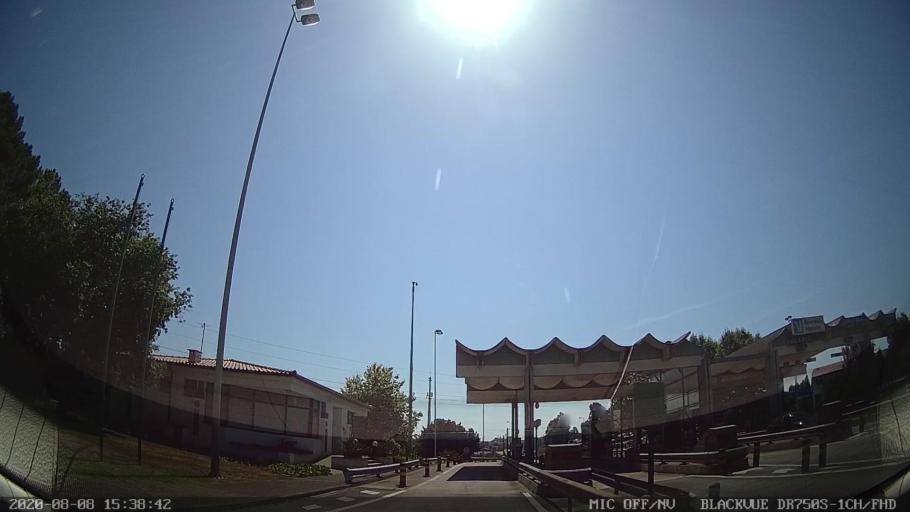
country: PT
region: Porto
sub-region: Gondomar
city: Baguim do Monte
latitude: 41.2020
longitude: -8.5512
